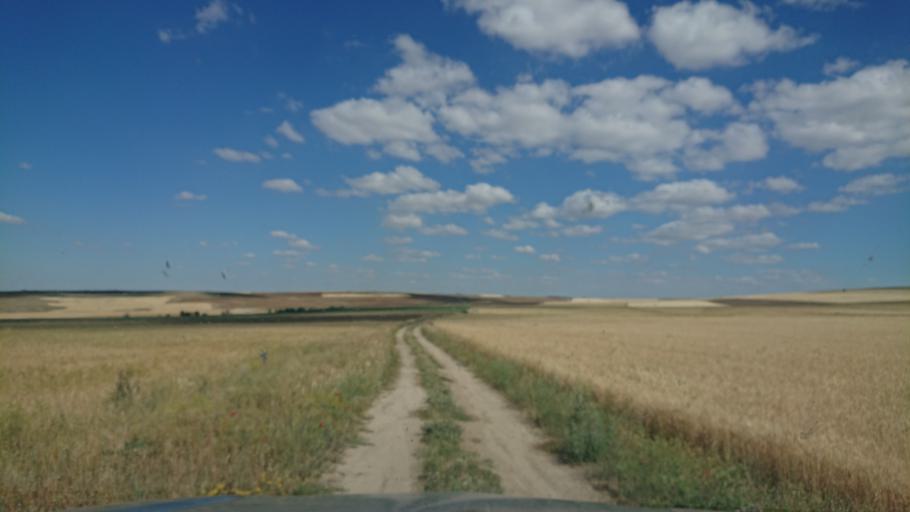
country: TR
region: Aksaray
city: Sariyahsi
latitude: 38.9399
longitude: 33.8344
